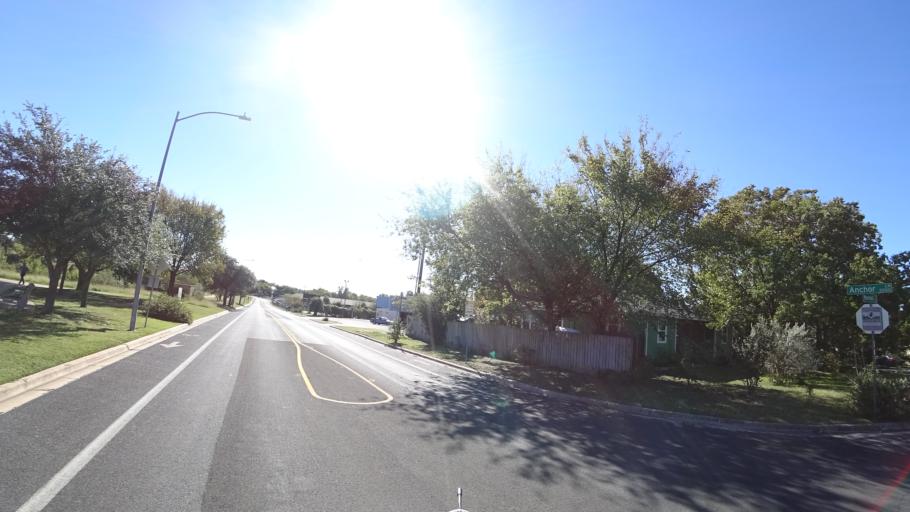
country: US
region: Texas
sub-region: Travis County
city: Austin
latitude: 30.2891
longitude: -97.7045
